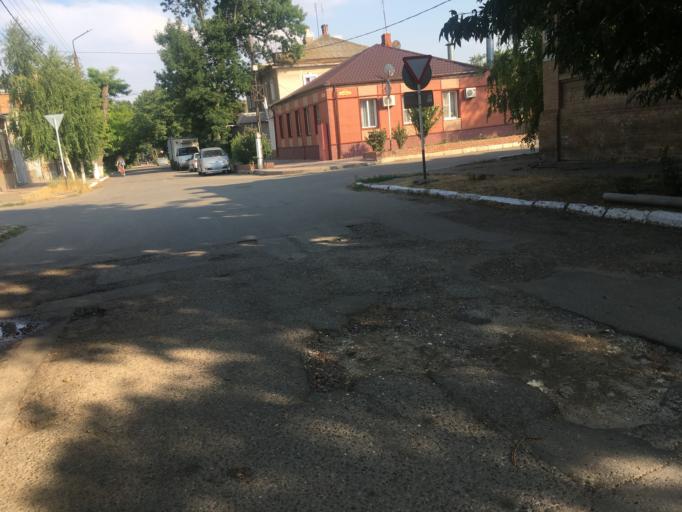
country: RU
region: Krasnodarskiy
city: Yeysk
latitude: 46.7155
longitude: 38.2728
